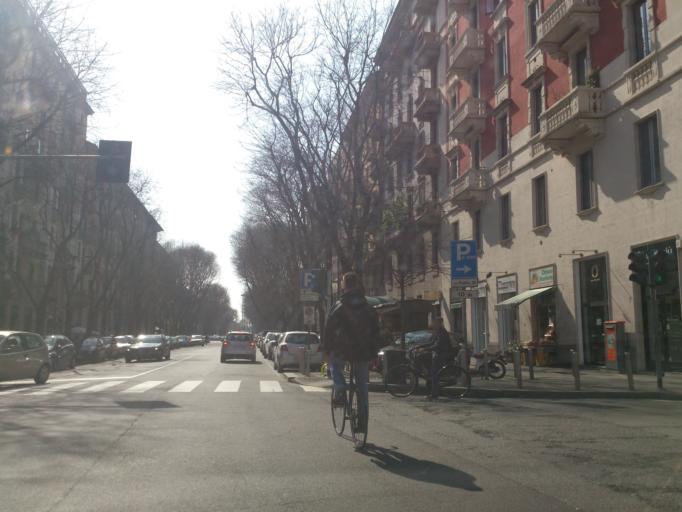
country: IT
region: Lombardy
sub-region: Citta metropolitana di Milano
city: Milano
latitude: 45.4578
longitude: 9.2129
